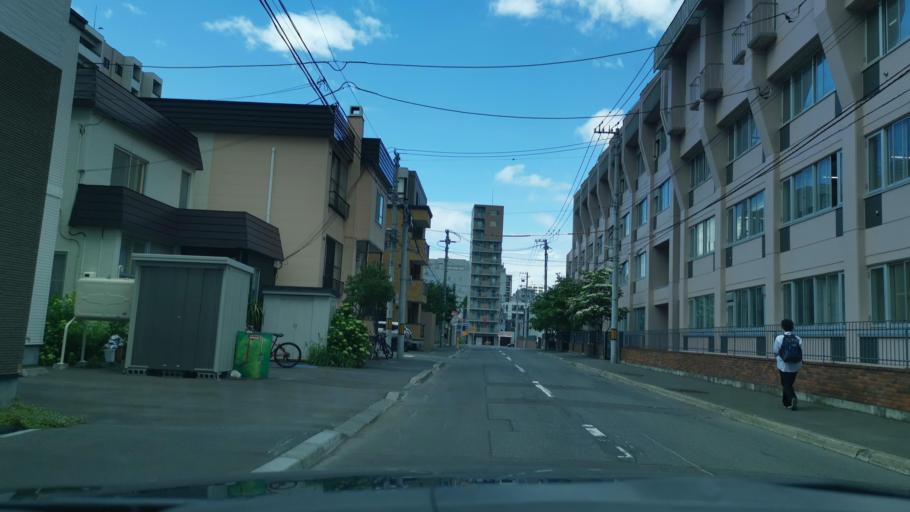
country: JP
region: Hokkaido
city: Sapporo
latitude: 43.0525
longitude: 141.3297
